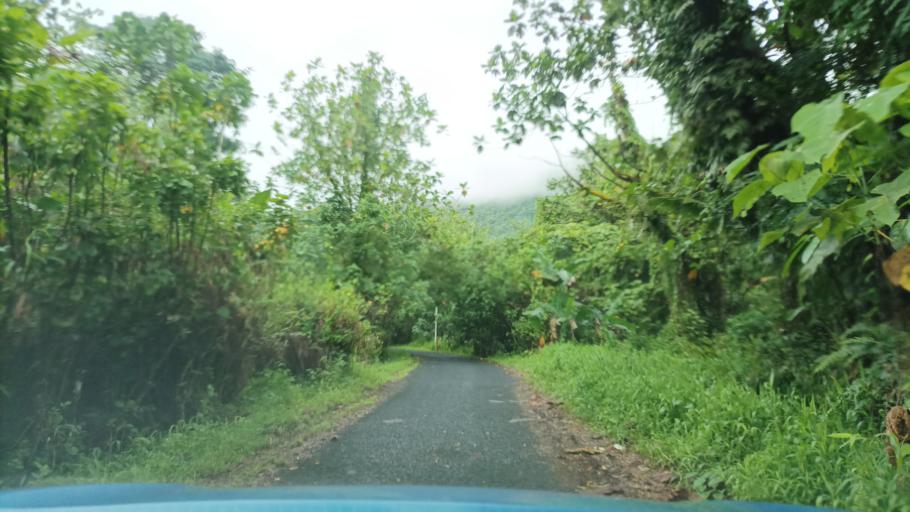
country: FM
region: Pohnpei
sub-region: Kolonia Municipality
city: Kolonia
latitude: 6.9213
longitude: 158.2780
